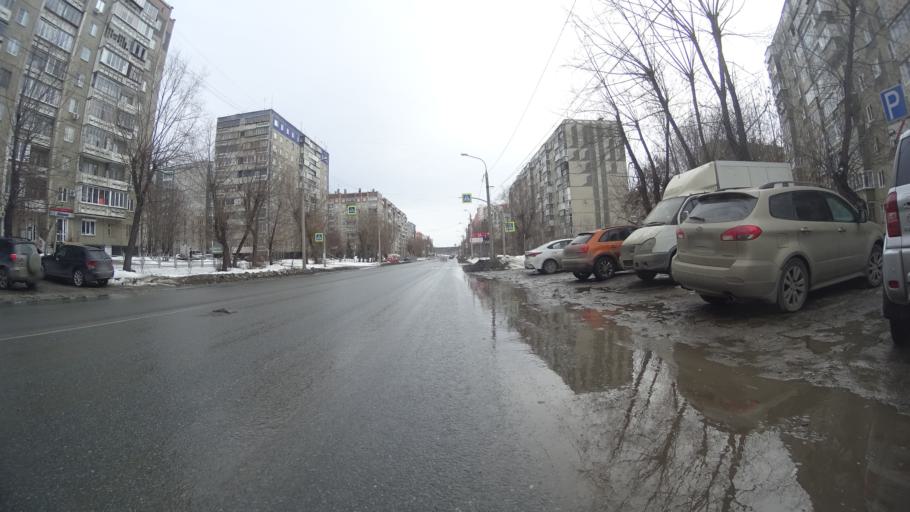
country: RU
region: Chelyabinsk
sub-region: Gorod Chelyabinsk
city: Chelyabinsk
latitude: 55.1798
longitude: 61.3072
